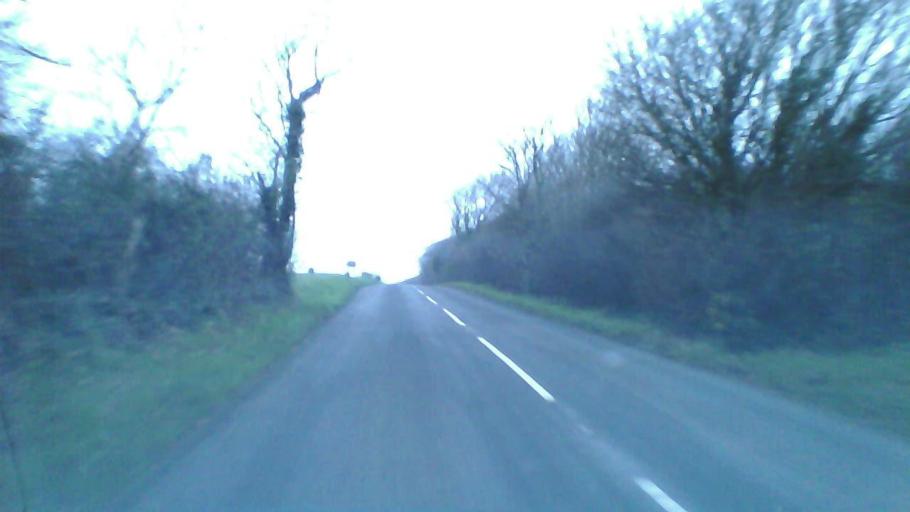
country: GB
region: England
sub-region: Isle of Wight
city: Brading
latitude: 50.6777
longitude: -1.1511
